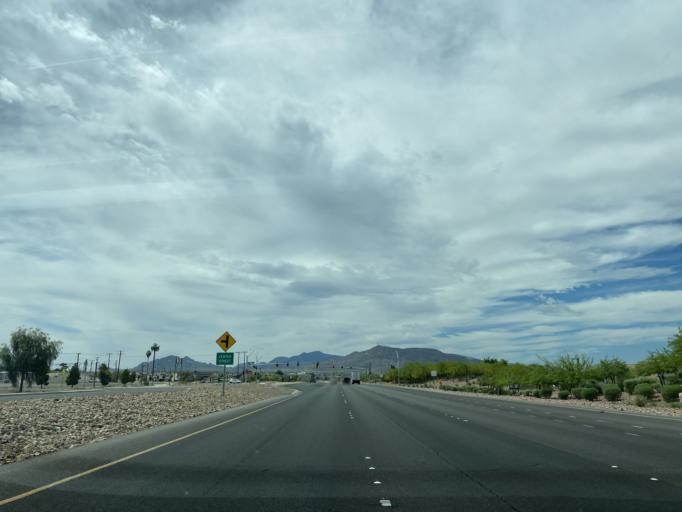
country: US
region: Nevada
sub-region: Clark County
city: Henderson
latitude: 36.0572
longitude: -114.9667
